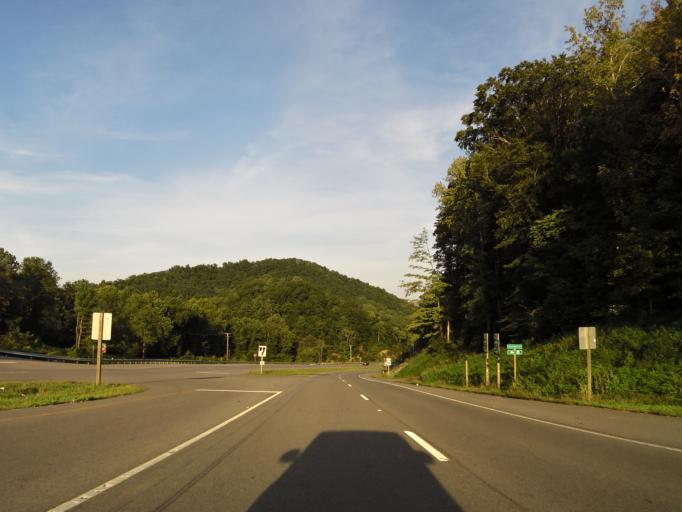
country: US
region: Virginia
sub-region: Washington County
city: Abingdon
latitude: 36.6941
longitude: -81.8978
